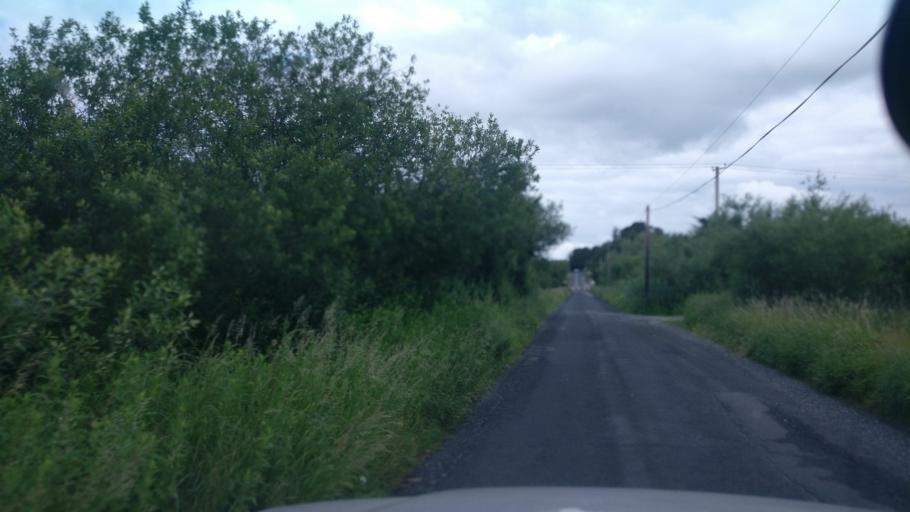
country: IE
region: Connaught
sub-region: County Galway
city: Loughrea
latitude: 53.1781
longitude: -8.5558
